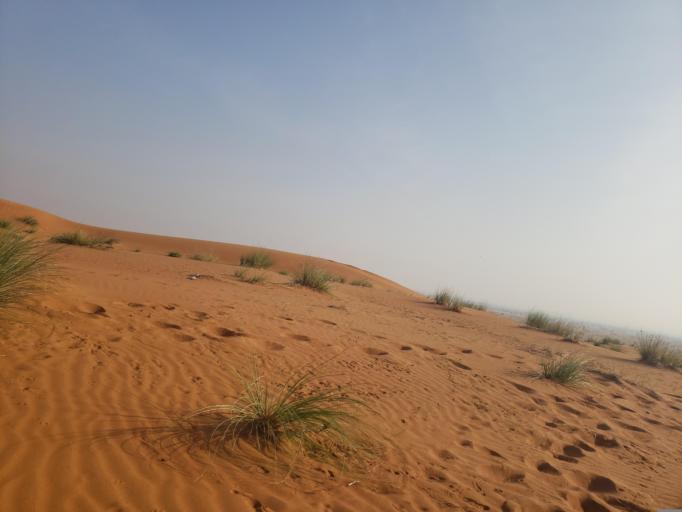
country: AE
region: Ash Shariqah
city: Adh Dhayd
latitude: 25.1382
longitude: 55.8420
